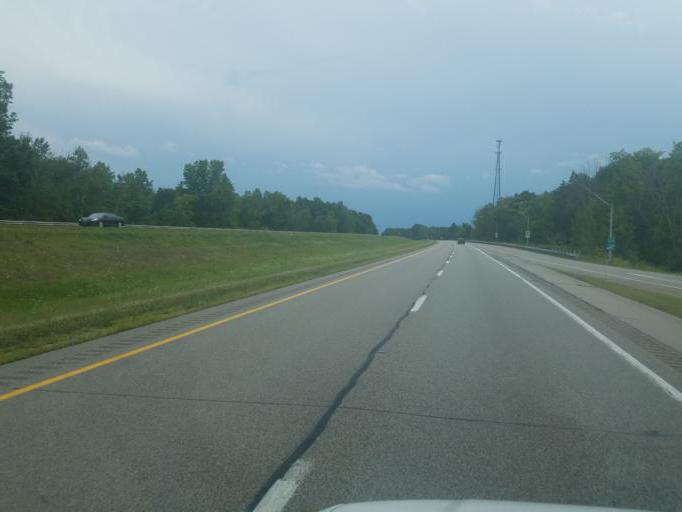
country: US
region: Pennsylvania
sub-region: Crawford County
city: Cochranton
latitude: 41.4666
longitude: -80.1668
